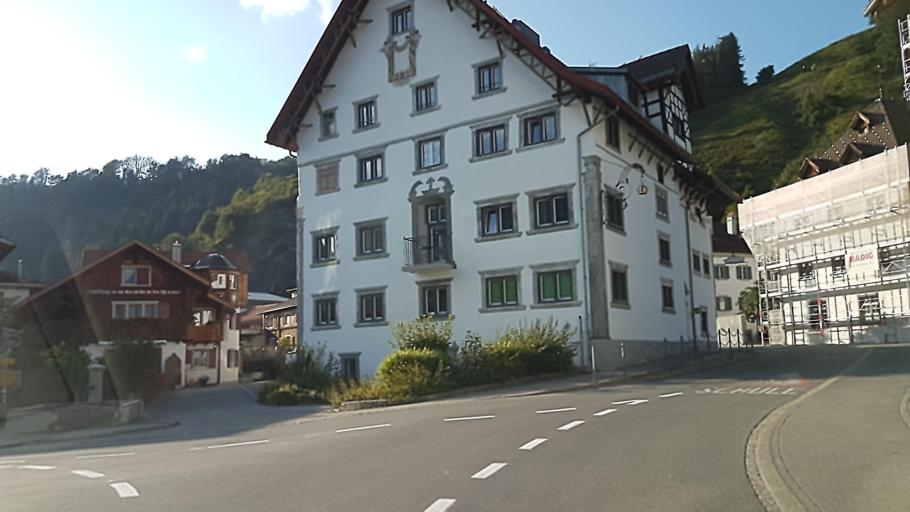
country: CH
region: Grisons
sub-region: Praettigau/Davos District
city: Grusch
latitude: 46.9816
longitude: 9.6482
